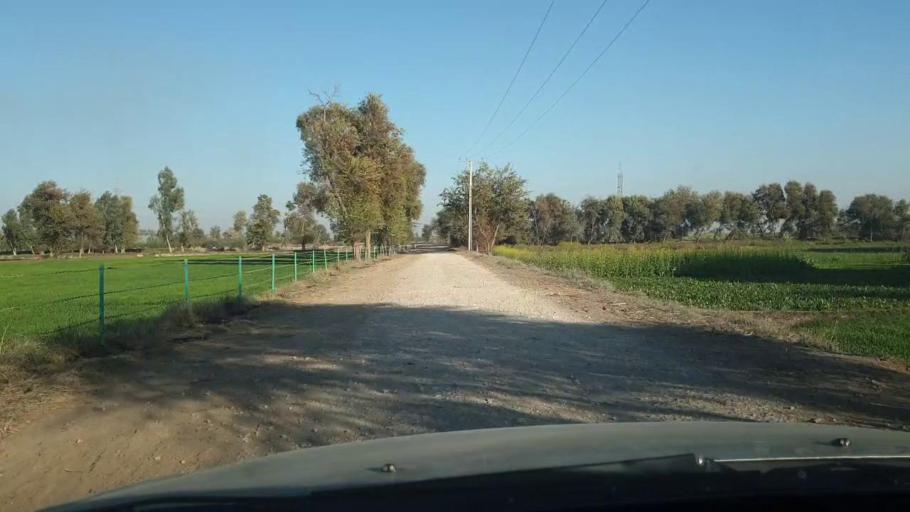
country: PK
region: Sindh
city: Ghotki
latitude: 28.0386
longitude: 69.3223
